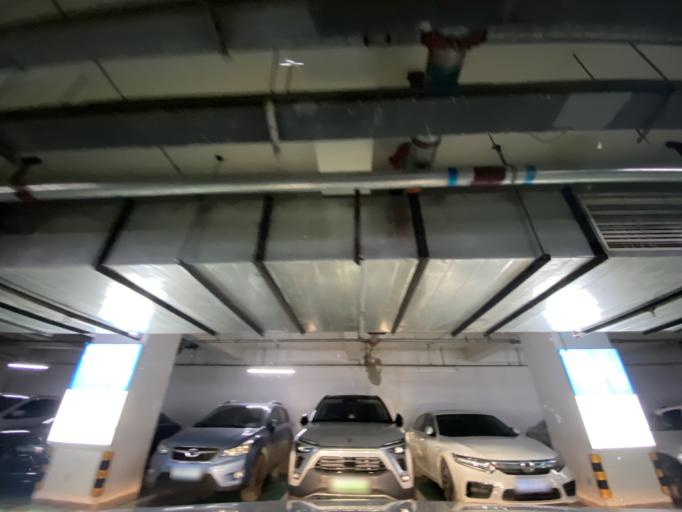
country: CN
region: Beijing
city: Haidian
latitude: 39.9785
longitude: 116.3082
